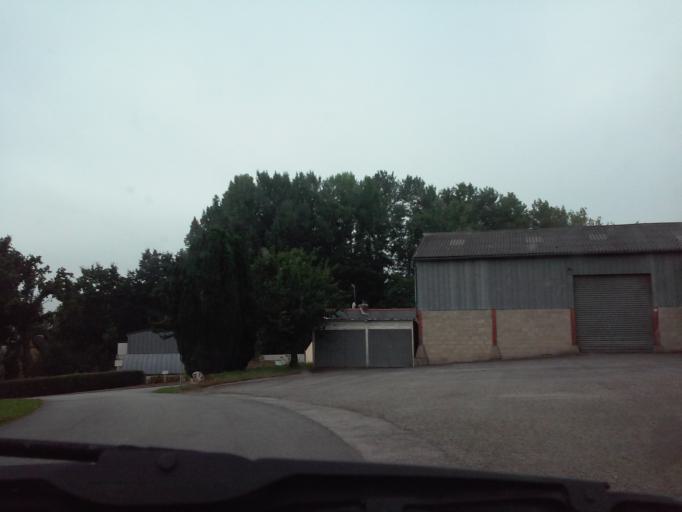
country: FR
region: Brittany
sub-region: Departement du Morbihan
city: Taupont
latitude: 48.0126
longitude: -2.4714
